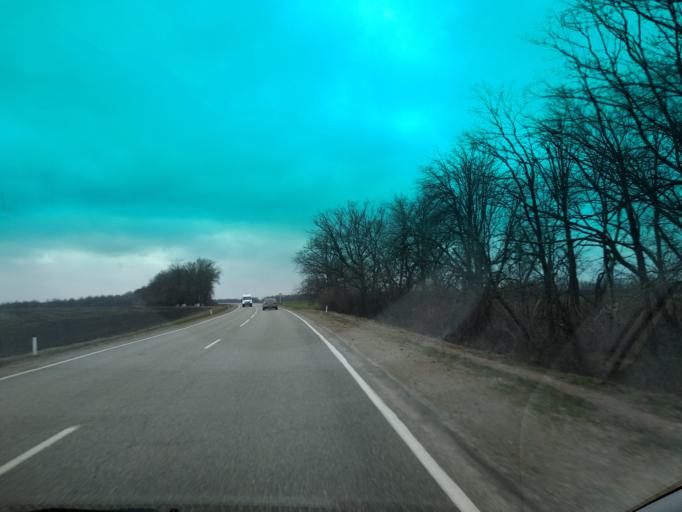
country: RU
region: Krasnodarskiy
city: Novorozhdestvenskaya
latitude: 45.7663
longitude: 39.9328
